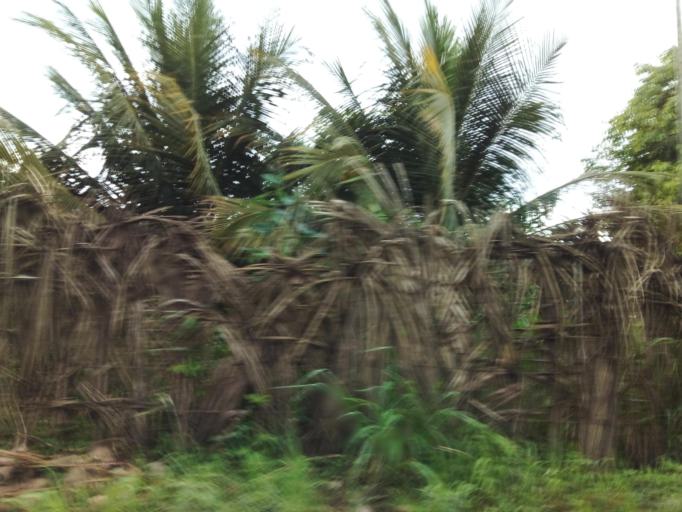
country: BR
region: Espirito Santo
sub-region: Marilandia
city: Marilandia
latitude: -19.5315
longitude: -40.4901
